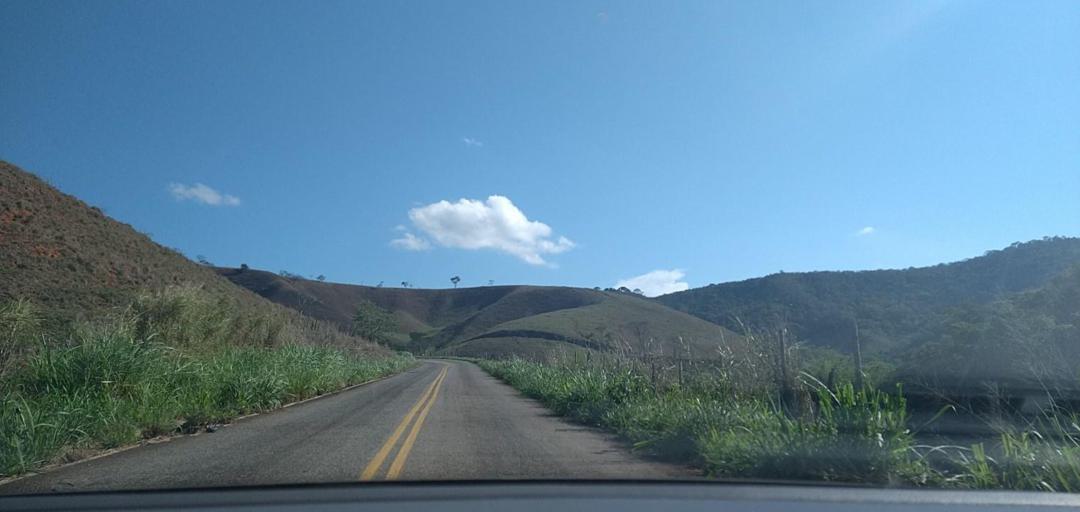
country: BR
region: Minas Gerais
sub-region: Alvinopolis
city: Alvinopolis
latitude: -20.1891
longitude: -42.9383
